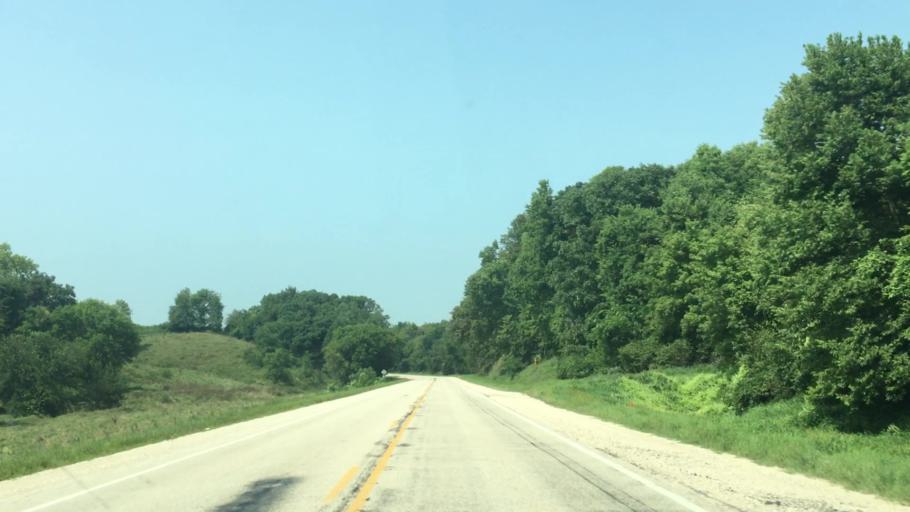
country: US
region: Iowa
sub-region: Fayette County
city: West Union
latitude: 43.0747
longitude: -91.8392
